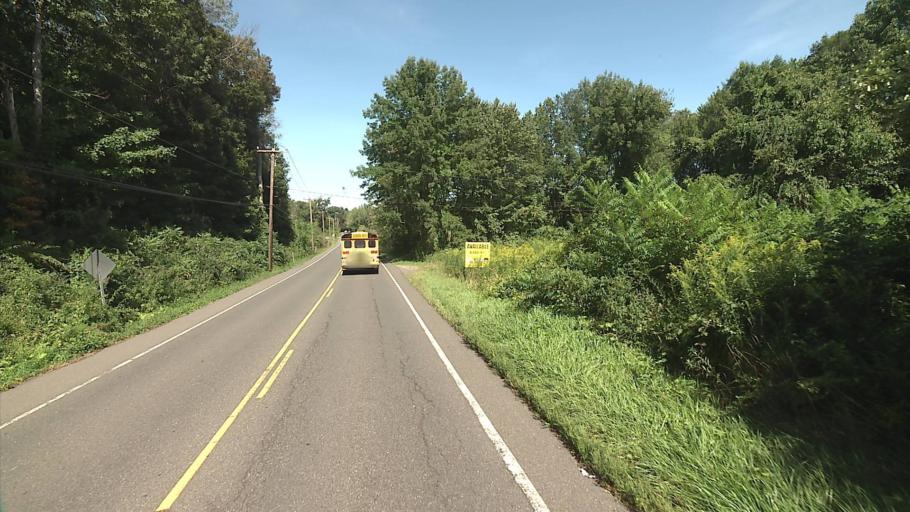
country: US
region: Connecticut
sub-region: New Haven County
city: Middlebury
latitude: 41.5033
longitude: -73.1514
